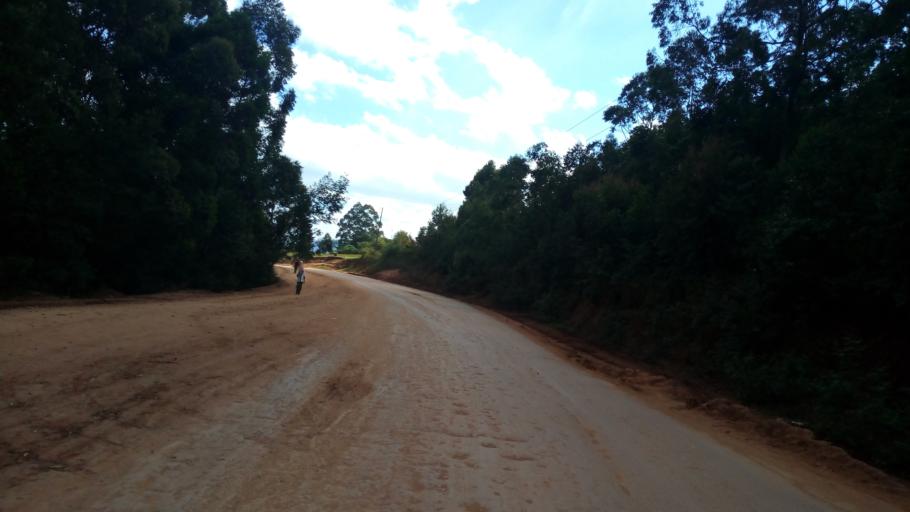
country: KE
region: Makueni
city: Wote
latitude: -1.6581
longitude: 37.4507
